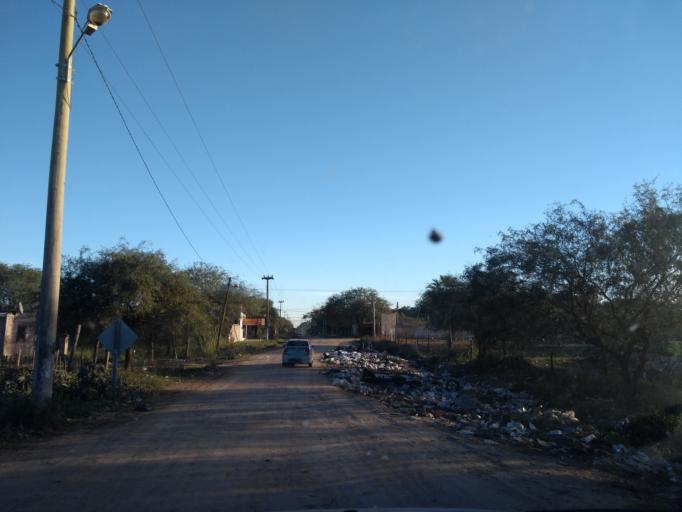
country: AR
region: Chaco
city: Puerto Vilelas
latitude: -27.4983
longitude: -58.9677
